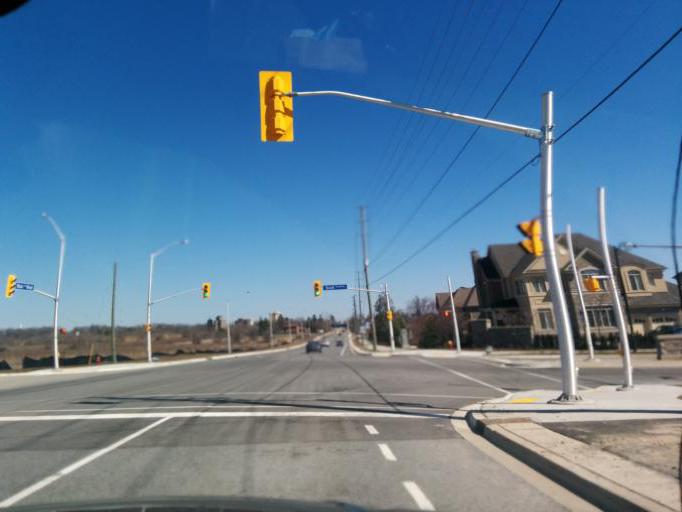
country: CA
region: Ontario
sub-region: Halton
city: Milton
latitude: 43.5037
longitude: -79.8933
